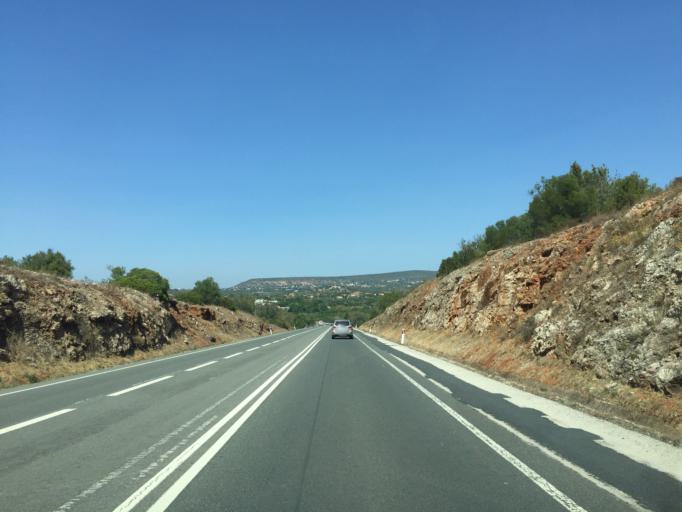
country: PT
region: Faro
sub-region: Silves
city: Sao Bartolomeu de Messines
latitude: 37.2037
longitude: -8.2594
